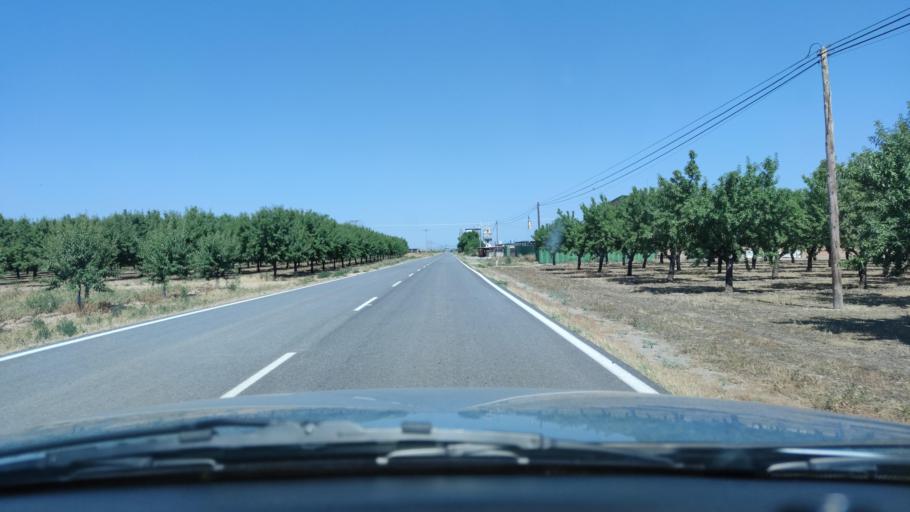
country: ES
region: Catalonia
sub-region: Provincia de Lleida
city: Ivars d'Urgell
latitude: 41.6885
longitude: 0.9697
